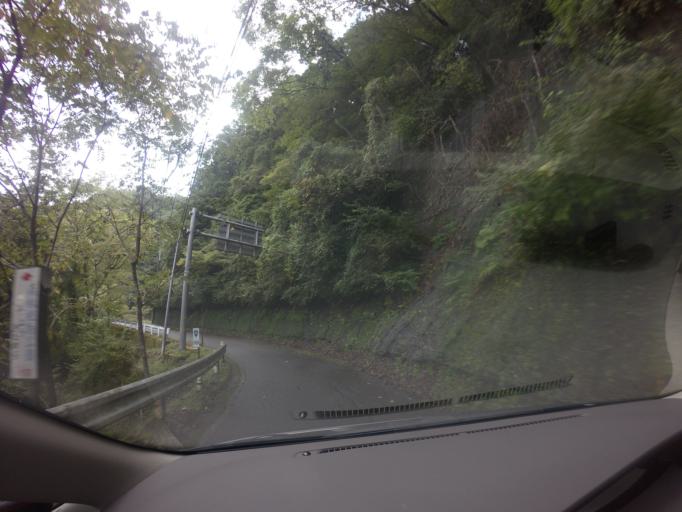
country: JP
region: Wakayama
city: Shingu
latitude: 33.9637
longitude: 135.8500
